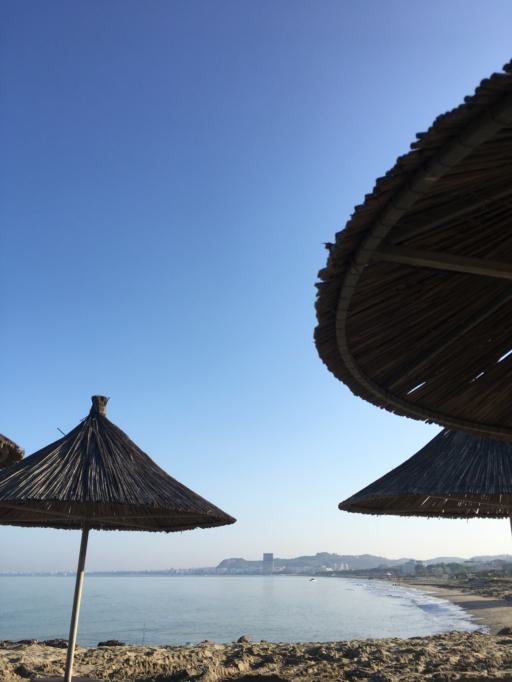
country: AL
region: Tirane
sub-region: Rrethi i Kavajes
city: Golem
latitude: 41.2430
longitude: 19.5176
